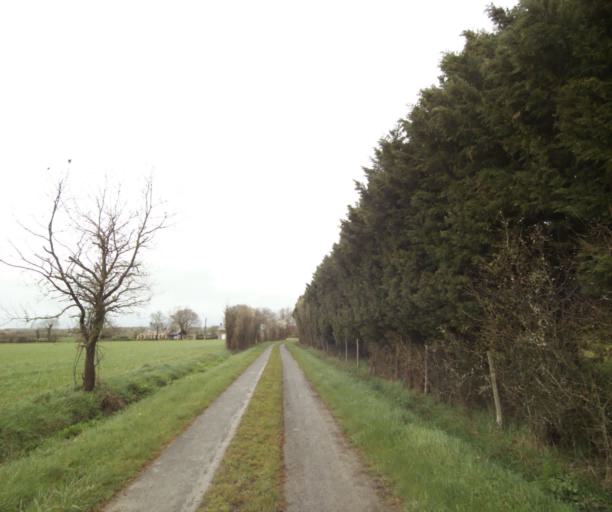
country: FR
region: Pays de la Loire
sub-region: Departement de la Loire-Atlantique
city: Bouvron
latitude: 47.4414
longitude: -1.8783
